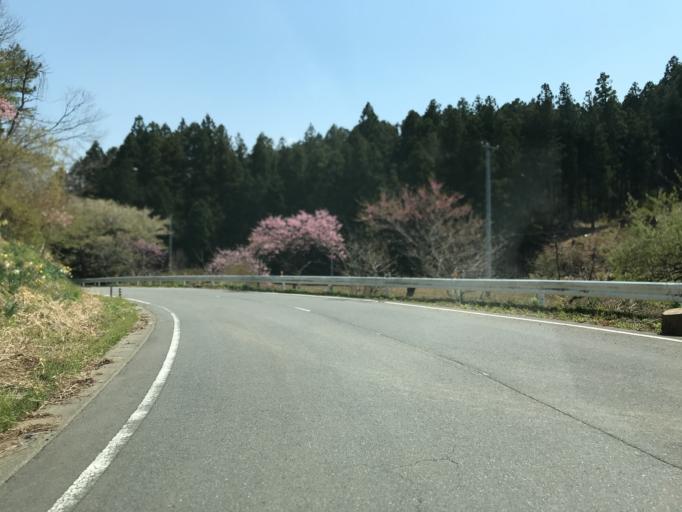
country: JP
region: Ibaraki
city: Kitaibaraki
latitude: 36.9708
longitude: 140.6438
